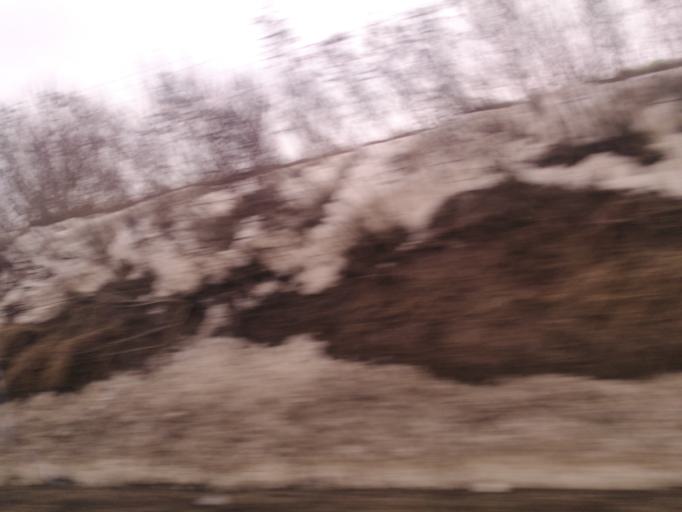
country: RO
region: Iasi
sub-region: Comuna Targu Frumos
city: Targu Frumos
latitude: 47.2054
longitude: 26.9881
